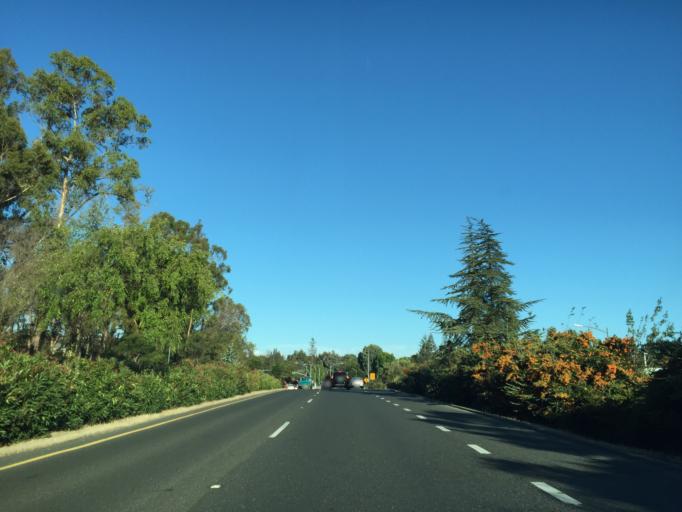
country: US
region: California
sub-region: Santa Clara County
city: Los Altos Hills
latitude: 37.4033
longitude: -122.1430
